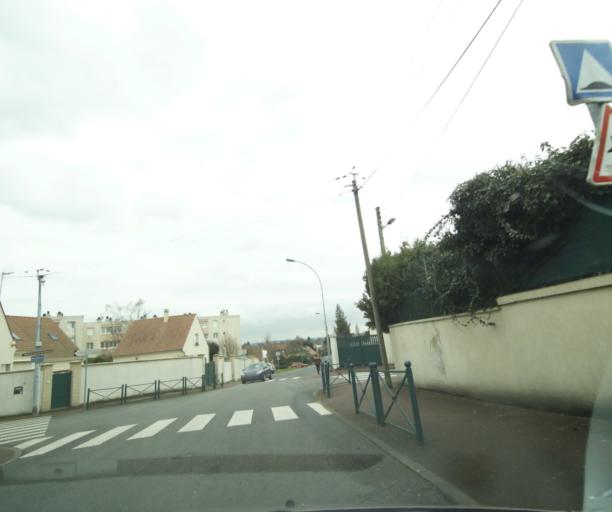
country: FR
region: Picardie
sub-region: Departement de l'Oise
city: Noyon
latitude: 49.5846
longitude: 3.0050
